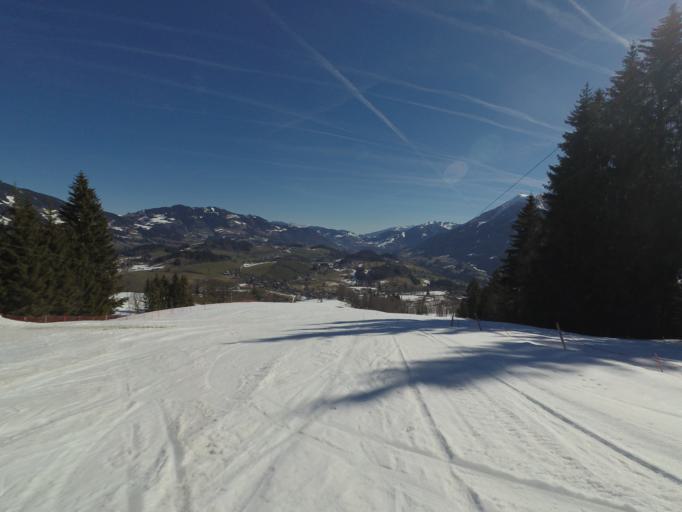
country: AT
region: Salzburg
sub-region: Politischer Bezirk Zell am See
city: Lend
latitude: 47.3097
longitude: 13.0706
